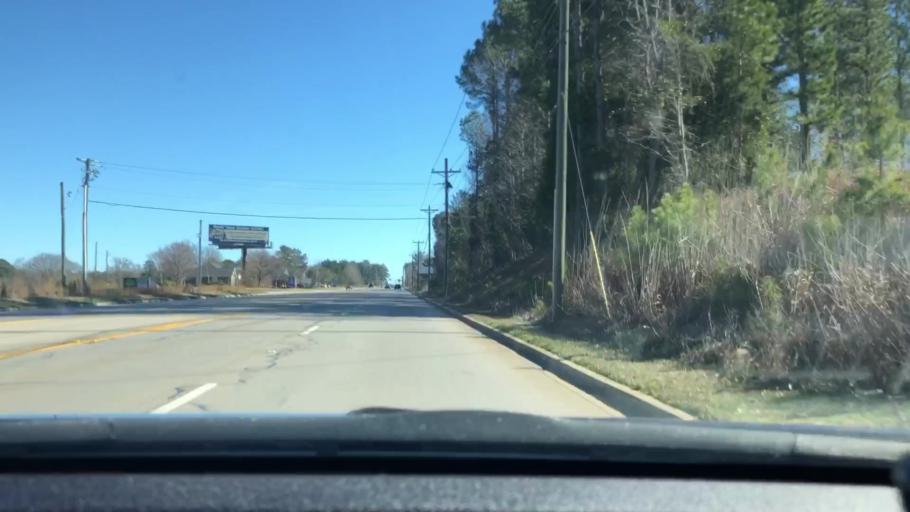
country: US
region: South Carolina
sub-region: Lexington County
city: Oak Grove
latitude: 34.0132
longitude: -81.1682
